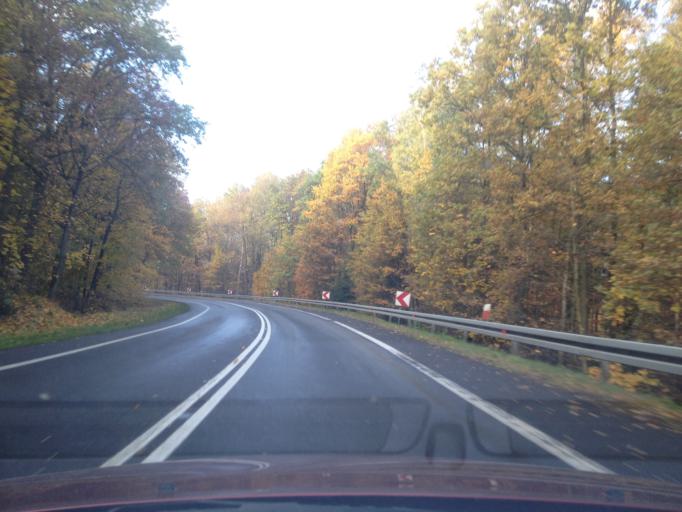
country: PL
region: Lower Silesian Voivodeship
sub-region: Powiat lubanski
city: Siekierczyn
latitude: 51.1614
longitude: 15.1456
